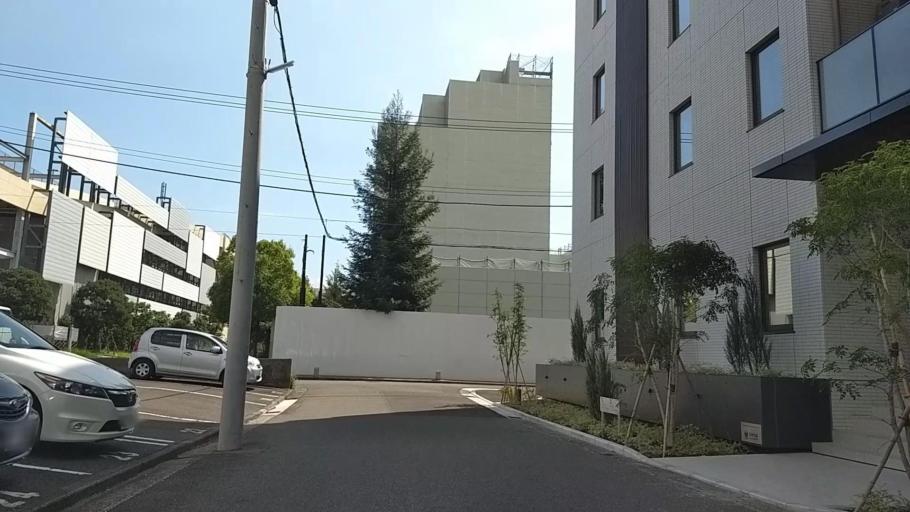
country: JP
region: Kanagawa
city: Yokohama
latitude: 35.5193
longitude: 139.5649
